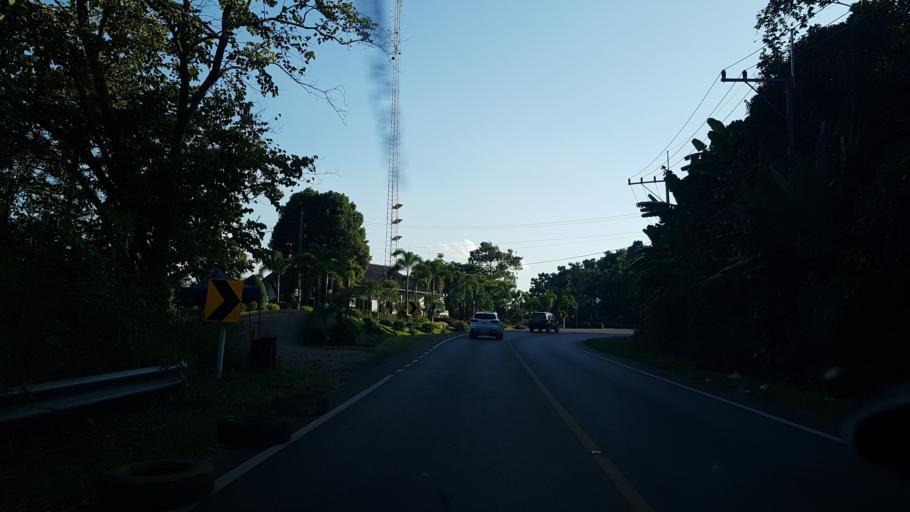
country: TH
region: Chiang Rai
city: Mae Fa Luang
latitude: 20.3002
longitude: 99.8162
